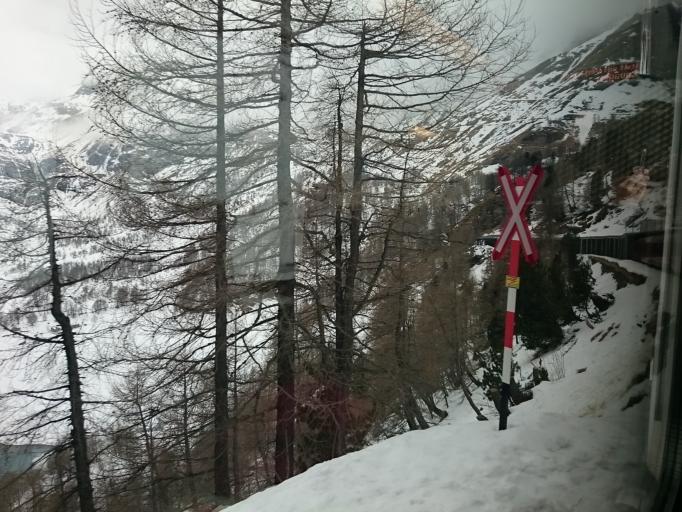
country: CH
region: Grisons
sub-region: Bernina District
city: Poschiavo
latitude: 46.3746
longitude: 10.0304
